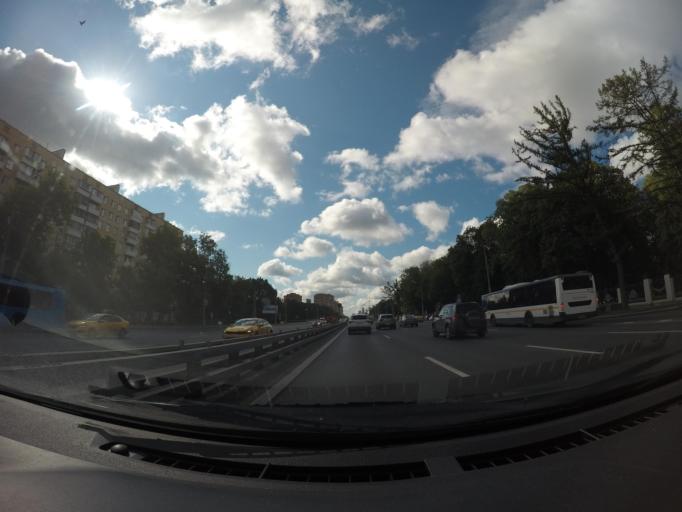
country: RU
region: Moskovskaya
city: Levoberezhnyy
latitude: 55.8546
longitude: 37.4706
